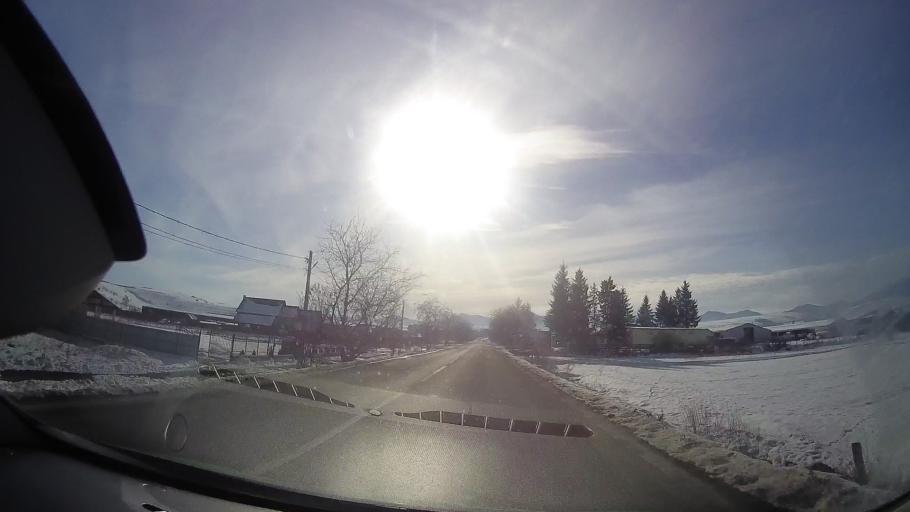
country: RO
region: Neamt
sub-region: Comuna Baltatesti
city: Valea Seaca
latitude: 47.1438
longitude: 26.3194
